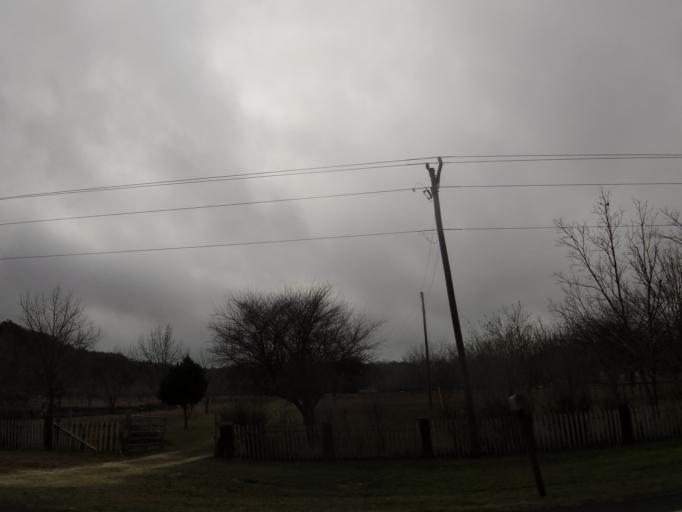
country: US
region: Florida
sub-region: Alachua County
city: High Springs
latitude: 29.8218
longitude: -82.6395
